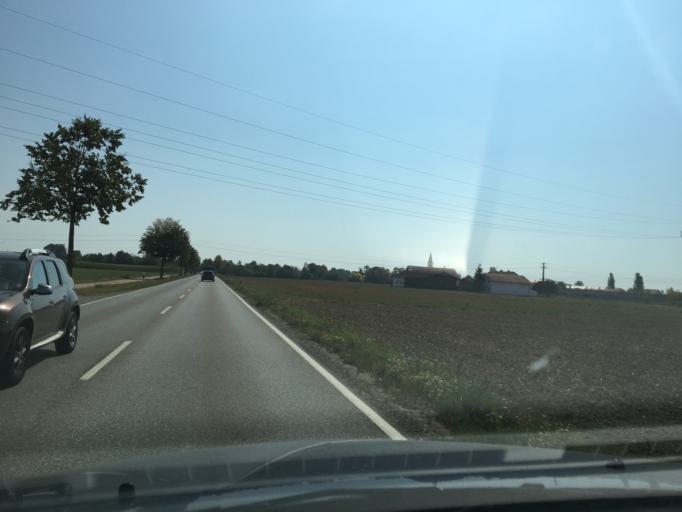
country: DE
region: Bavaria
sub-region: Upper Bavaria
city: Mettenheim
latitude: 48.2507
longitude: 12.4813
